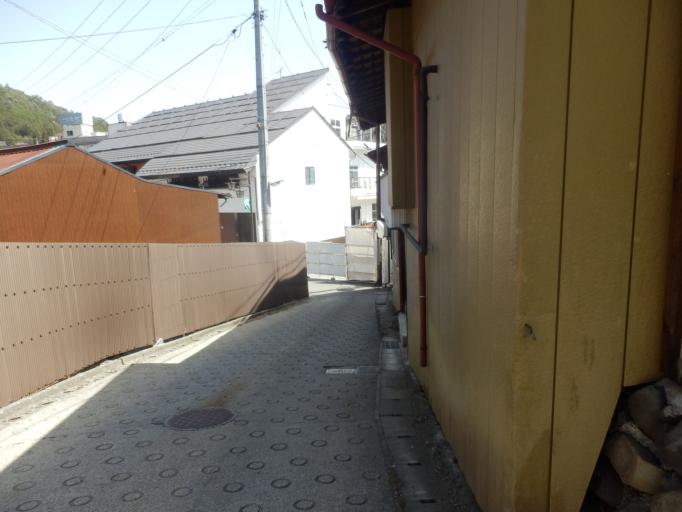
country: JP
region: Nagano
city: Ina
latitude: 35.8497
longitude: 137.6968
